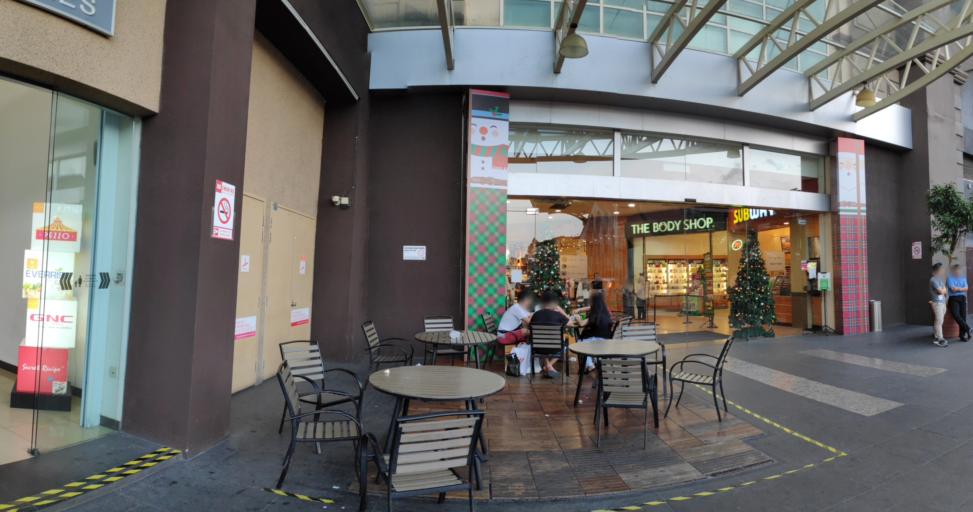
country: MY
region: Sarawak
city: Kuching
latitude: 1.5590
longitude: 110.3442
